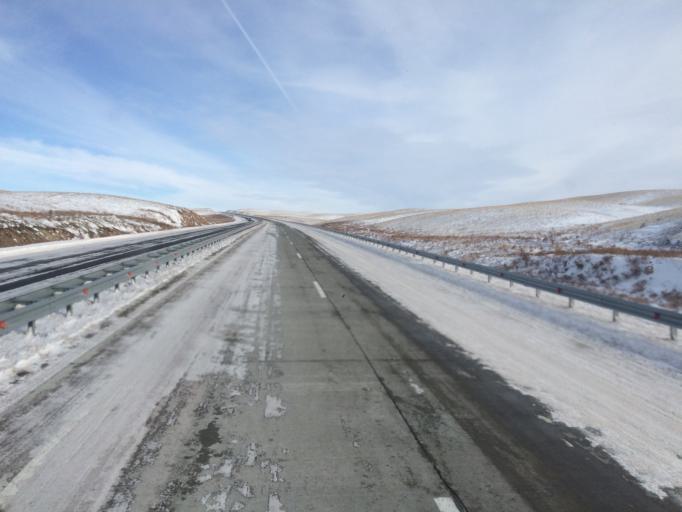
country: KZ
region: Zhambyl
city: Georgiyevka
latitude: 43.3900
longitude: 74.8032
